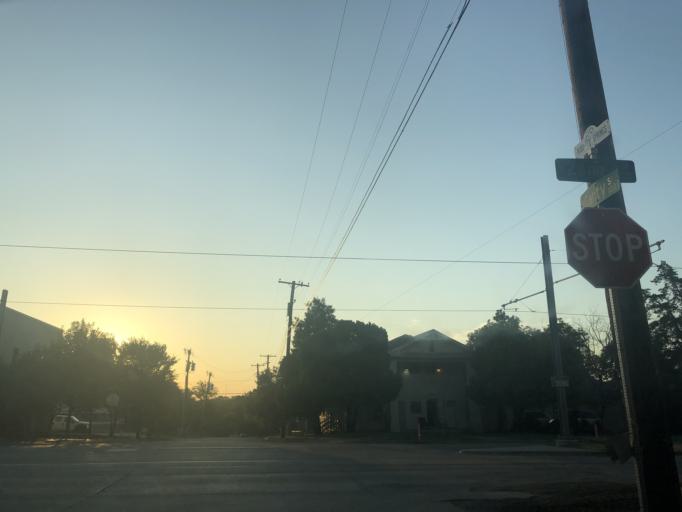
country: US
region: Texas
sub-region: Dallas County
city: Dallas
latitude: 32.7522
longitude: -96.8244
